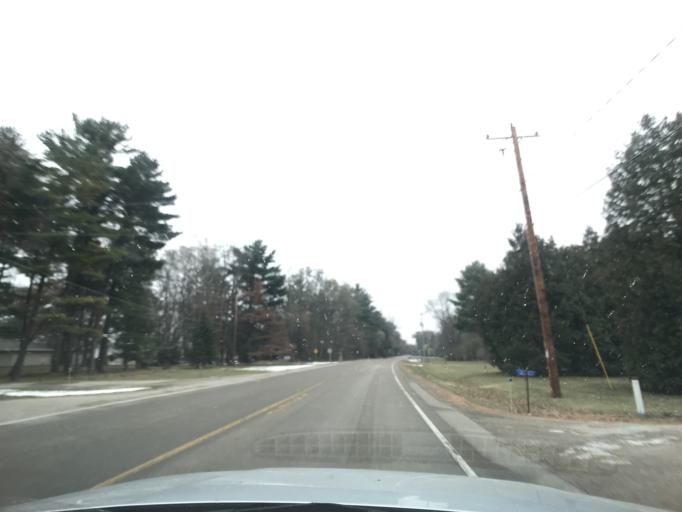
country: US
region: Wisconsin
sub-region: Marinette County
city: Marinette
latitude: 45.0629
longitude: -87.6194
